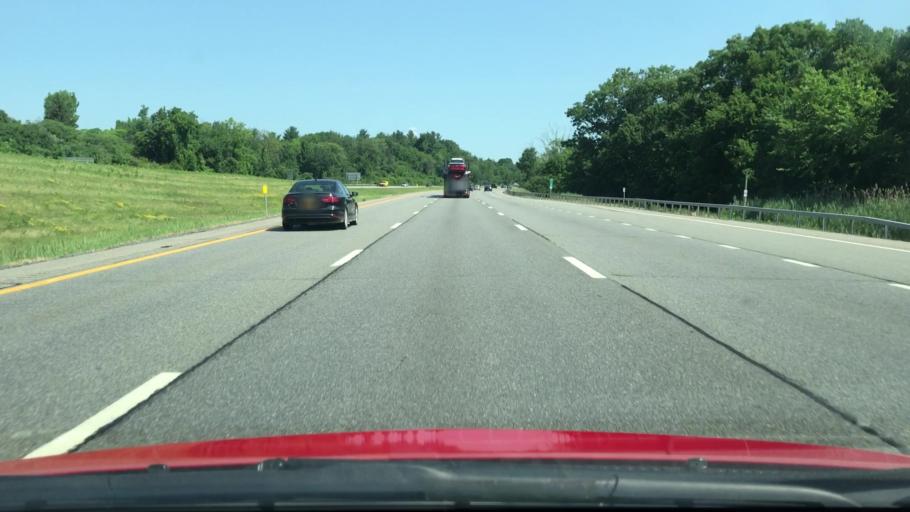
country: US
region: New York
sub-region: Saratoga County
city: Country Knolls
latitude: 42.9428
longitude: -73.8050
